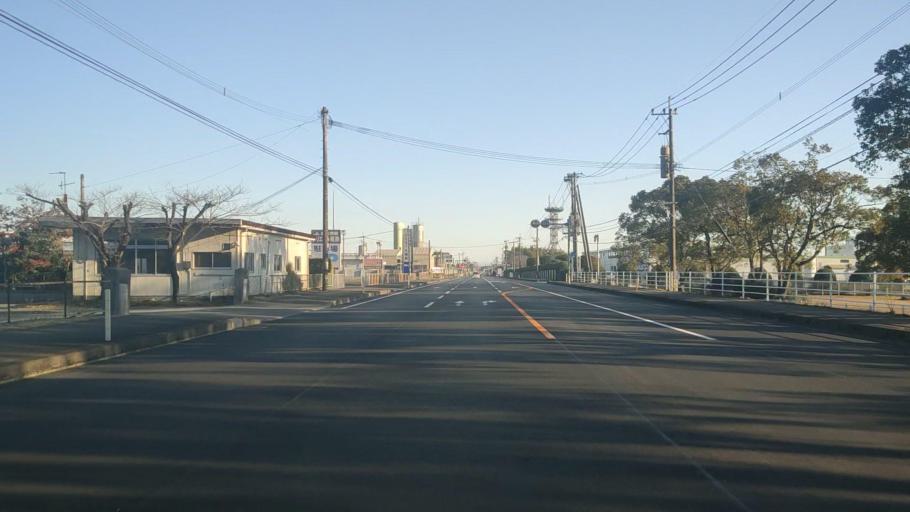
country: JP
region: Miyazaki
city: Takanabe
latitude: 32.2219
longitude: 131.5423
